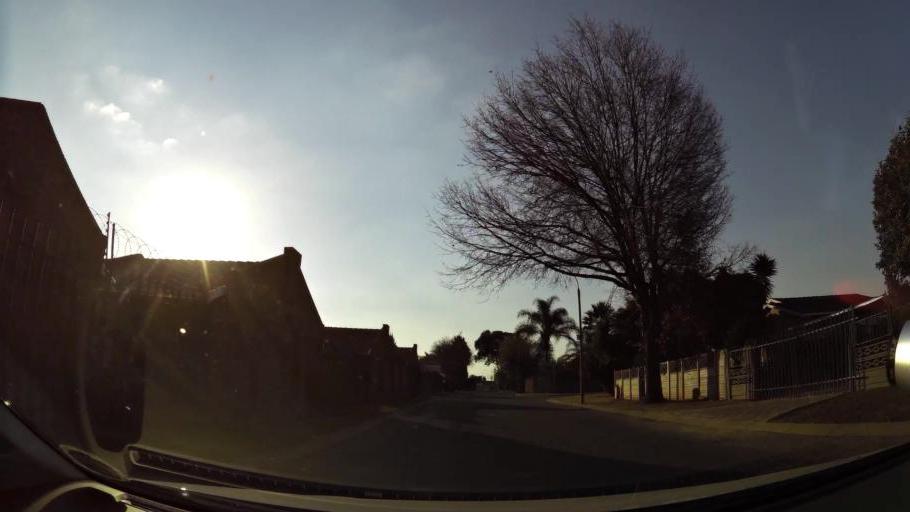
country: ZA
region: Gauteng
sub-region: City of Johannesburg Metropolitan Municipality
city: Modderfontein
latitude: -26.0686
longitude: 28.2198
